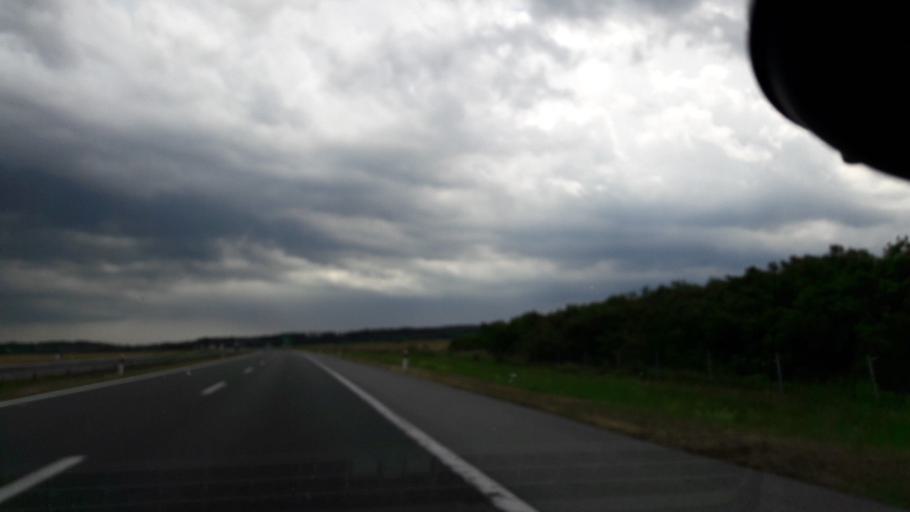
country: HR
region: Brodsko-Posavska
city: Batrina
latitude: 45.1746
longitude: 17.6554
